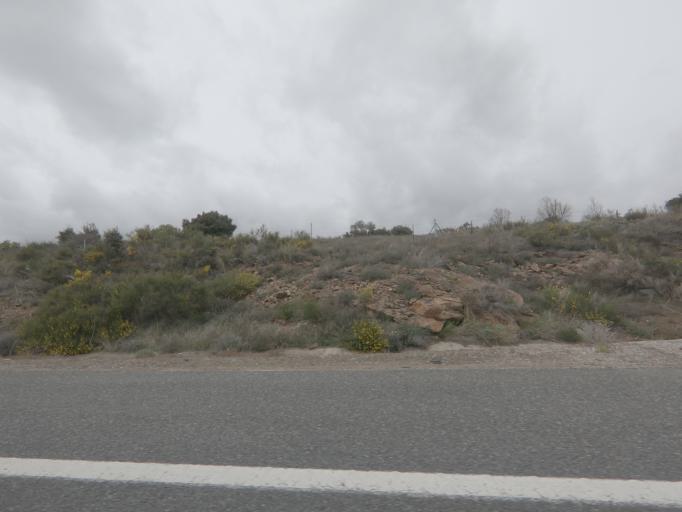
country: ES
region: Castille and Leon
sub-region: Provincia de Salamanca
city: Bejar
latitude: 40.3945
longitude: -5.7598
